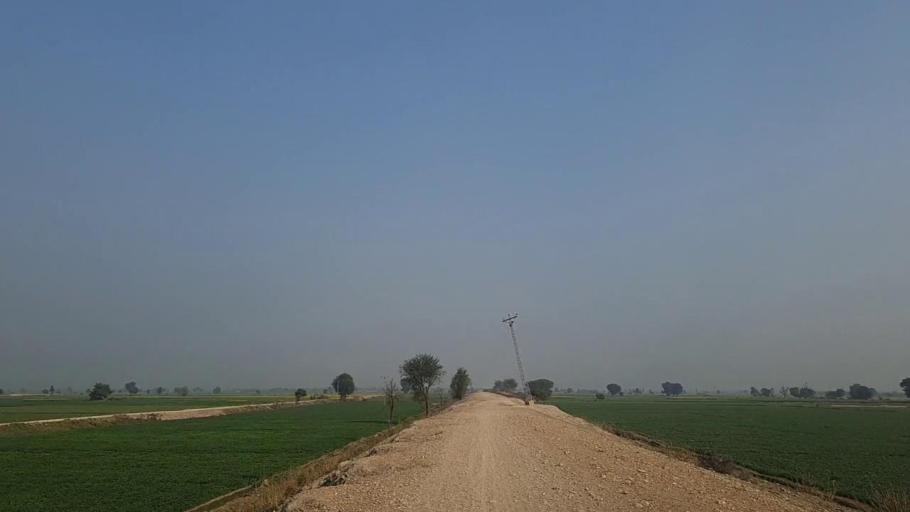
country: PK
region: Sindh
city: Sann
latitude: 26.0857
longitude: 68.1627
